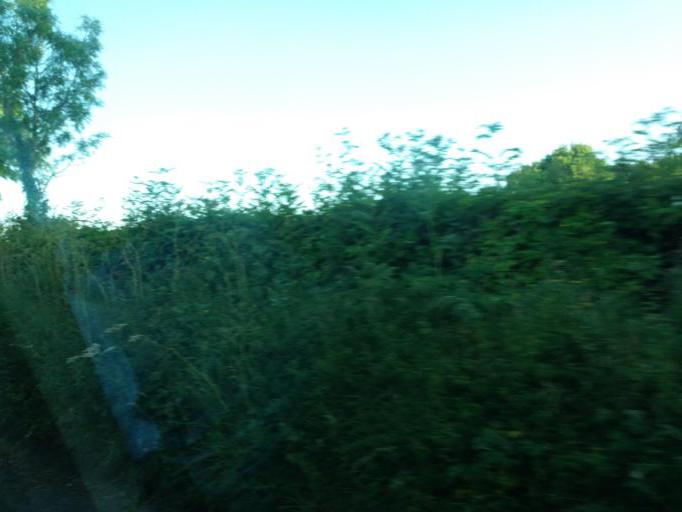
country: IE
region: Leinster
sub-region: An Mhi
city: Ashbourne
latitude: 53.5743
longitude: -6.3550
